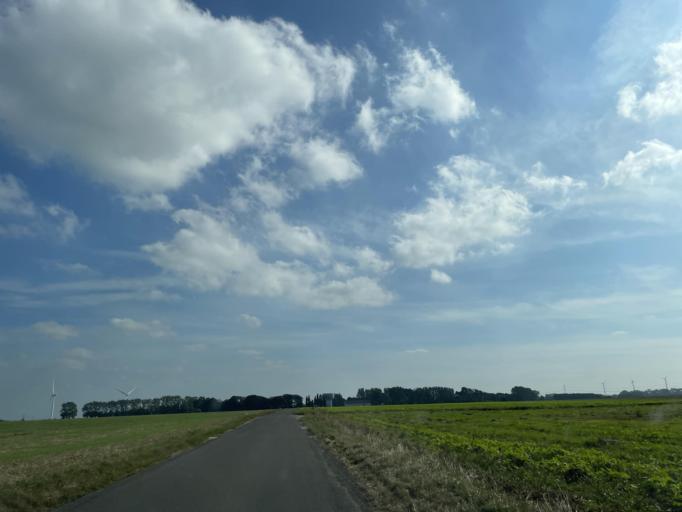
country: FR
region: Haute-Normandie
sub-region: Departement de la Seine-Maritime
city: Criel-sur-Mer
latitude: 50.0343
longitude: 1.3447
